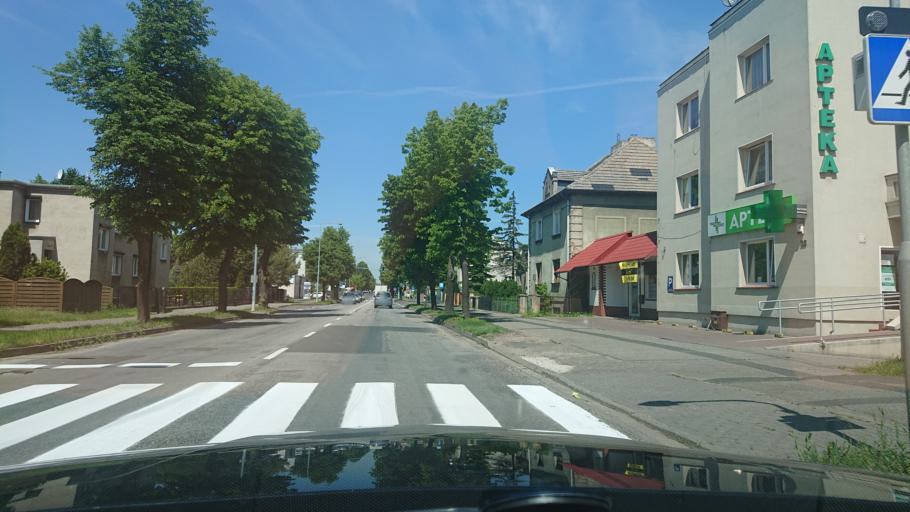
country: PL
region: Greater Poland Voivodeship
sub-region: Powiat gnieznienski
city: Gniezno
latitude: 52.5233
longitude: 17.6021
